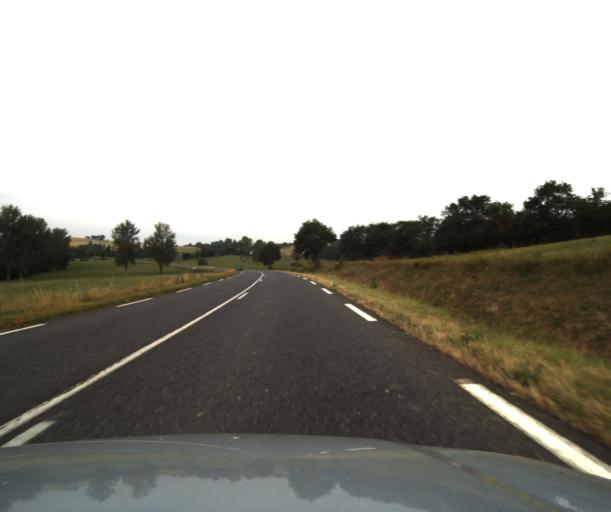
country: FR
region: Midi-Pyrenees
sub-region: Departement du Gers
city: Pavie
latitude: 43.5626
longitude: 0.5053
